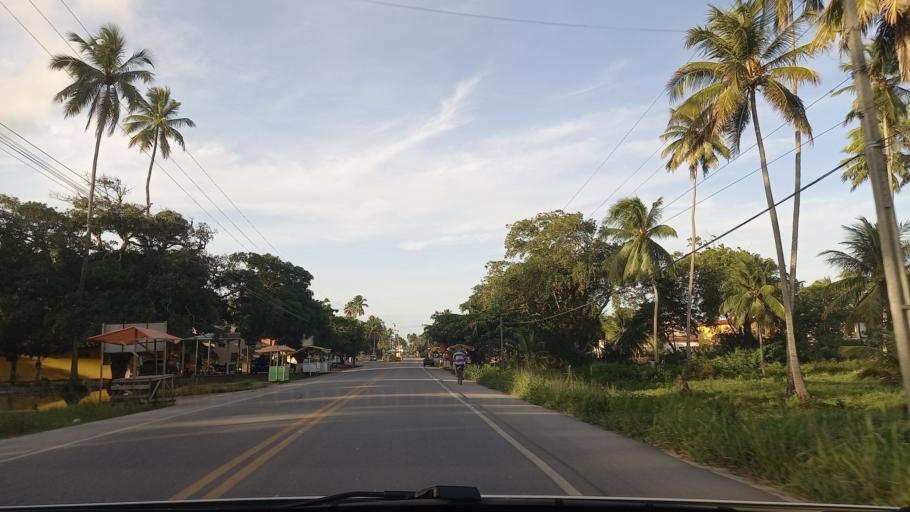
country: BR
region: Pernambuco
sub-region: Sao Jose Da Coroa Grande
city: Sao Jose da Coroa Grande
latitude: -8.9212
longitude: -35.1575
